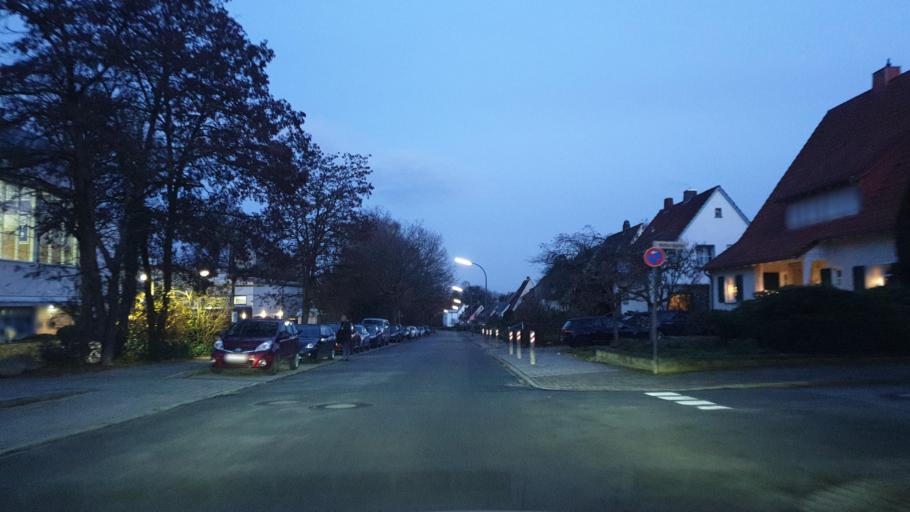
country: DE
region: Lower Saxony
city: Osnabrueck
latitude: 52.2687
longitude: 8.0077
